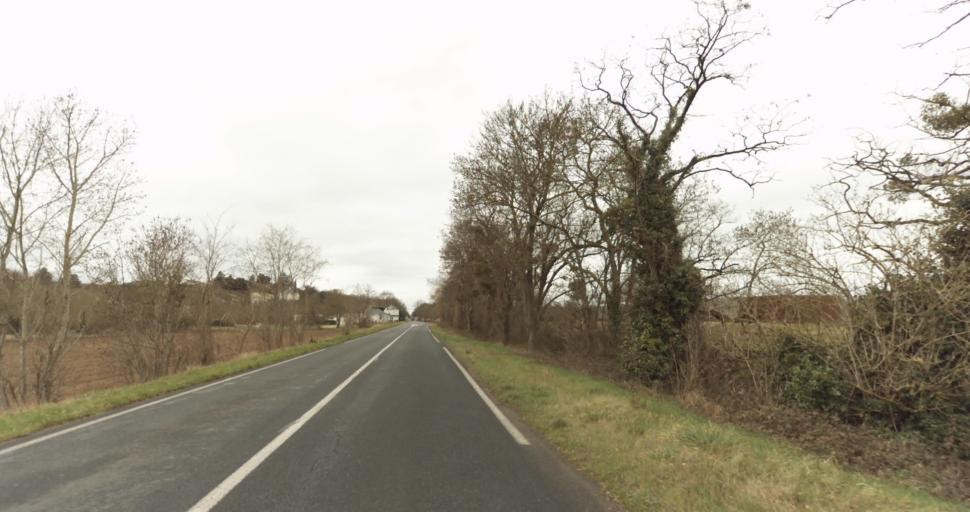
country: FR
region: Pays de la Loire
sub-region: Departement de Maine-et-Loire
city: Varennes-sur-Loire
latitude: 47.2278
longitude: 0.0217
